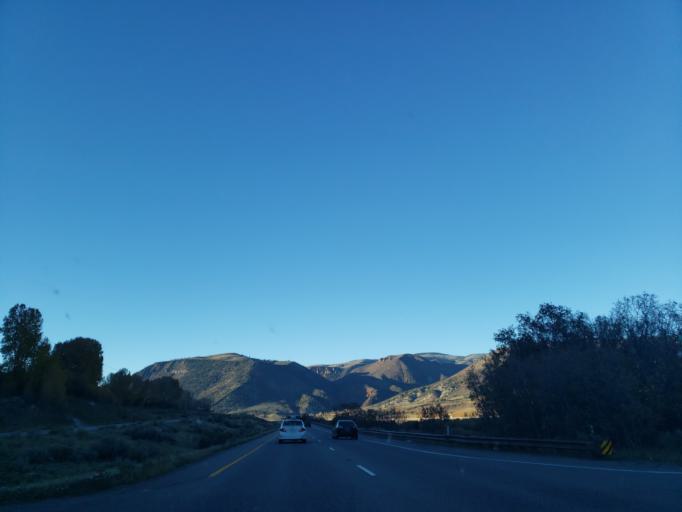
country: US
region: Colorado
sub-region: Pitkin County
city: Snowmass Village
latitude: 39.2686
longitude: -106.8903
